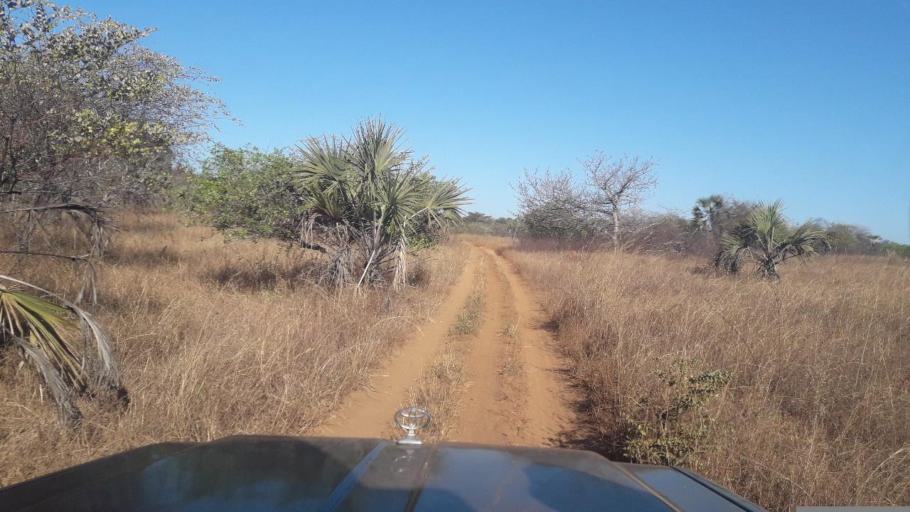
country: MG
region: Boeny
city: Sitampiky
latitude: -16.4120
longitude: 45.6033
